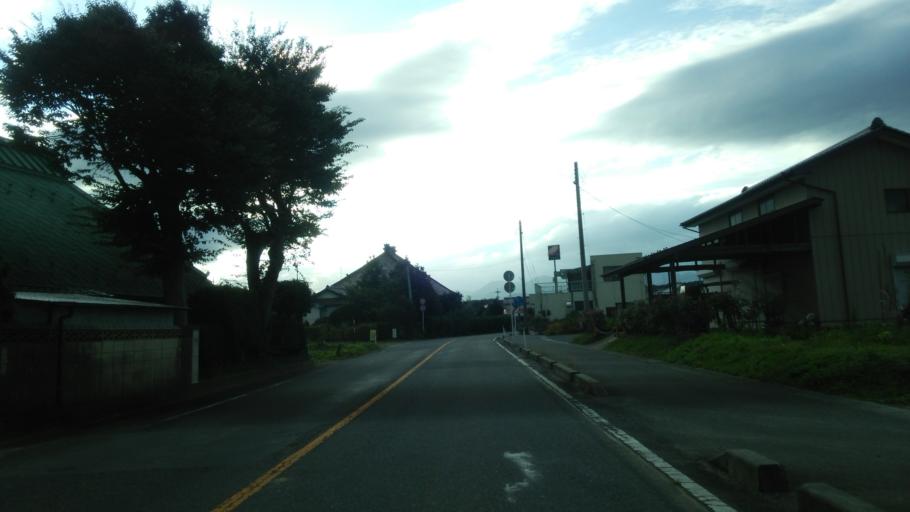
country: JP
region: Fukushima
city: Sukagawa
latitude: 37.3307
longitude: 140.2961
